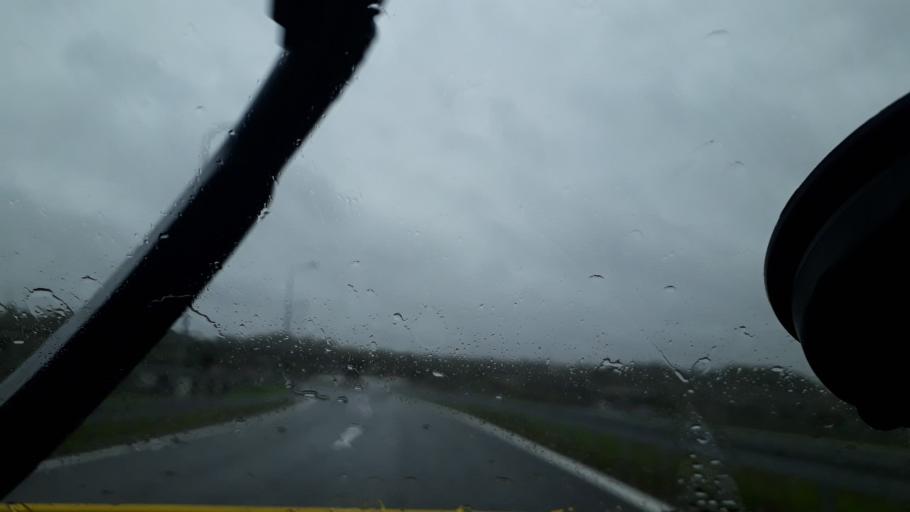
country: BA
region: Republika Srpska
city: Laktasi
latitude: 44.9202
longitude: 17.3005
